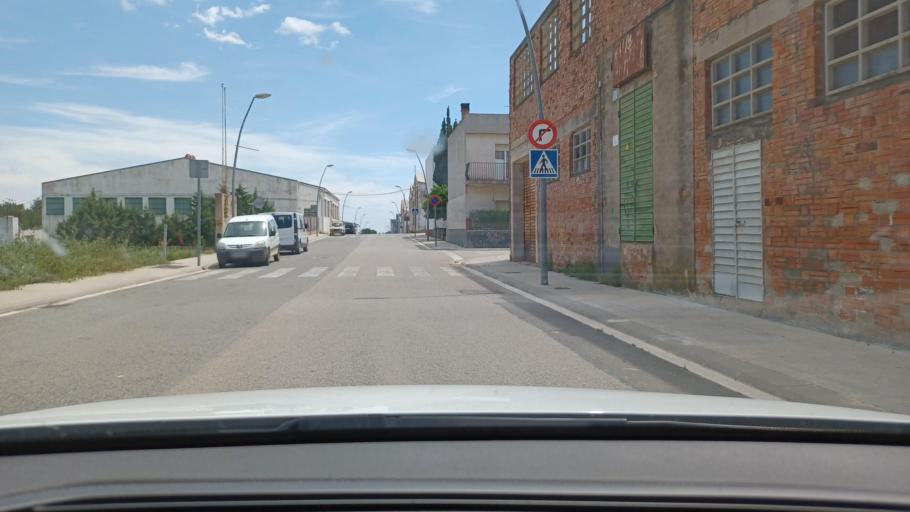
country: ES
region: Valencia
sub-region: Provincia de Castello
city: Rosell
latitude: 40.6346
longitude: 0.2875
